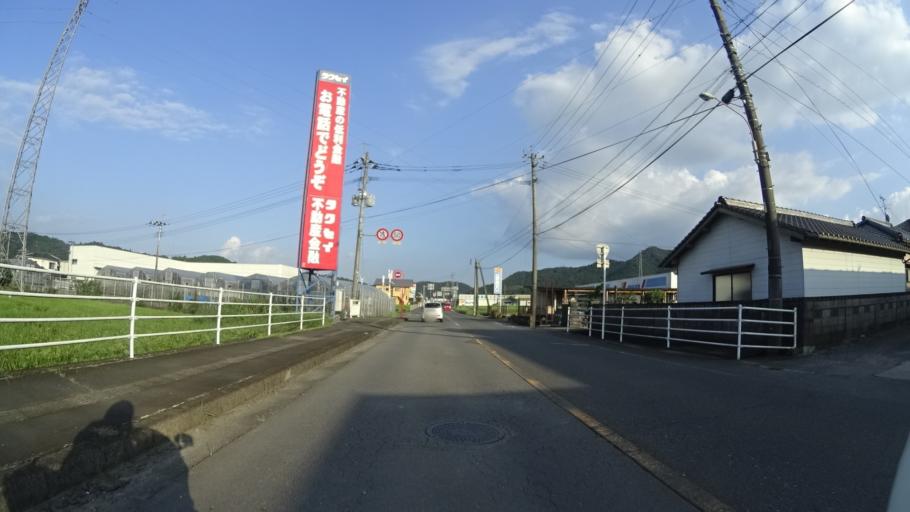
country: JP
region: Oita
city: Bungo-Takada-shi
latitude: 33.4372
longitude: 131.3596
